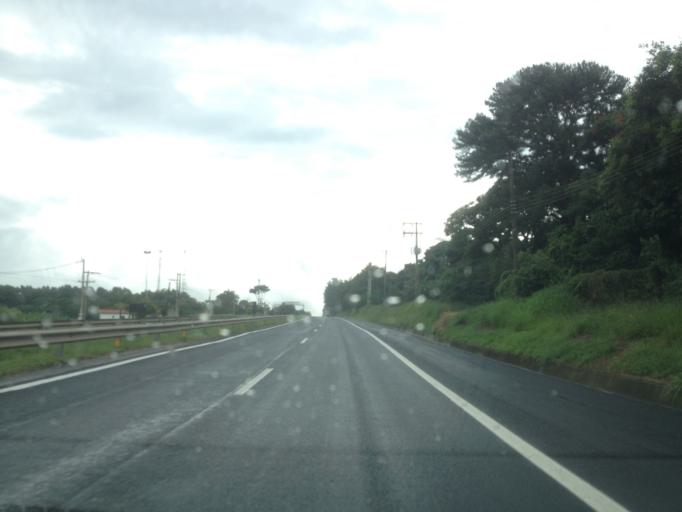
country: BR
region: Sao Paulo
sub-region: Itu
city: Itu
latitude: -23.2546
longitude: -47.3525
